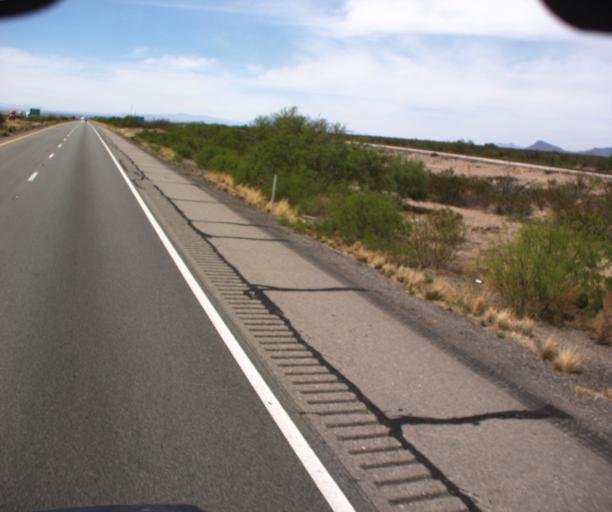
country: US
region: New Mexico
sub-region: Hidalgo County
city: Lordsburg
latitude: 32.2416
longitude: -109.1094
